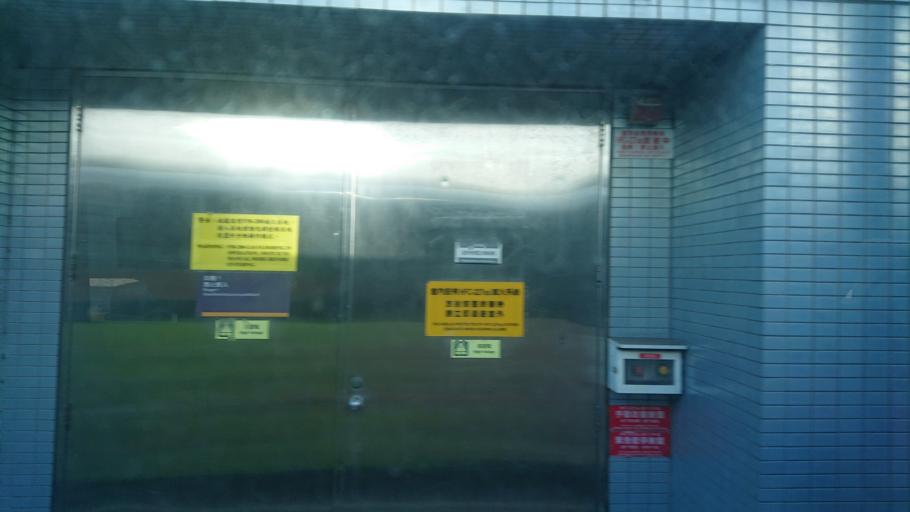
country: TW
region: Taiwan
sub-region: Chiayi
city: Taibao
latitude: 23.4595
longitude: 120.3235
